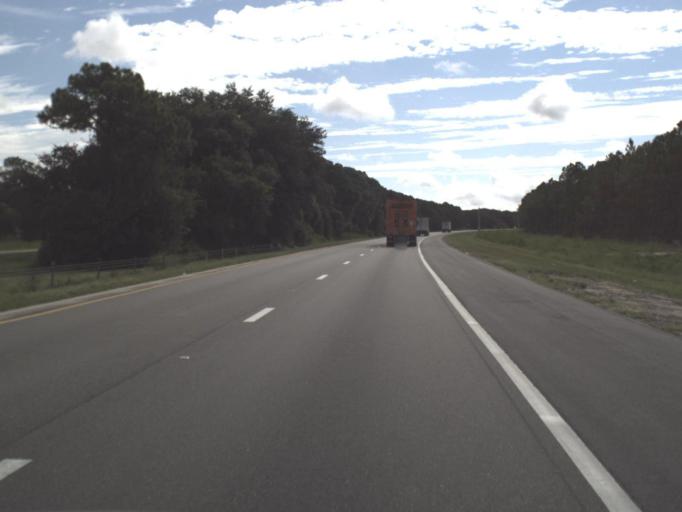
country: US
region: Florida
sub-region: Sarasota County
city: Plantation
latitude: 27.1120
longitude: -82.3298
